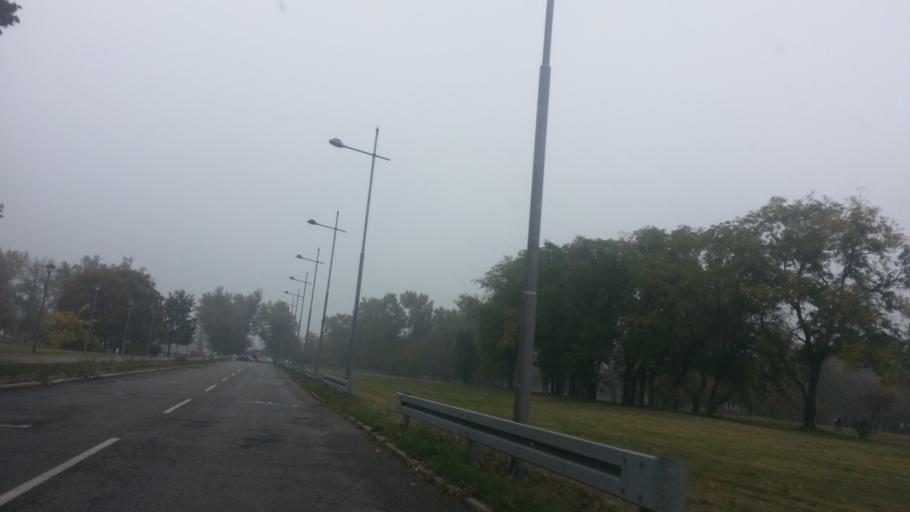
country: RS
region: Central Serbia
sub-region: Belgrade
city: Novi Beograd
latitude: 44.8199
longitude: 20.4390
